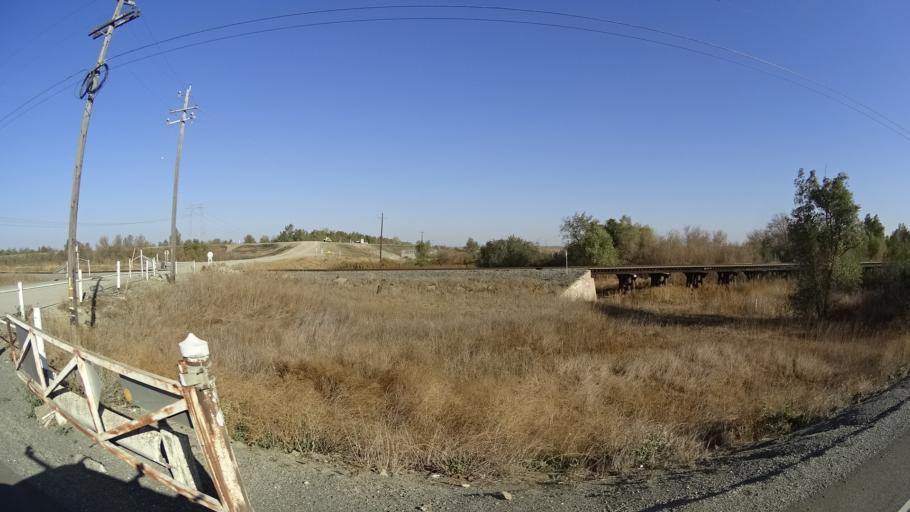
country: US
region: California
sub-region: Yolo County
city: Woodland
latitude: 38.6765
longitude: -121.6723
